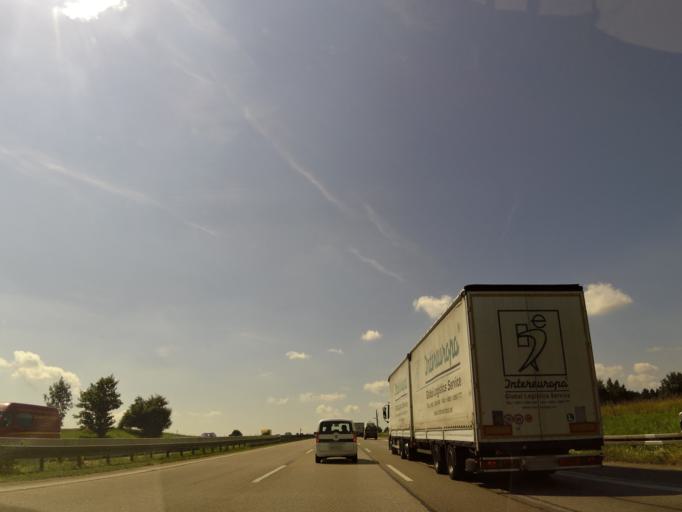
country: DE
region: Bavaria
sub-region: Upper Bavaria
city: Schweitenkirchen
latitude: 48.5457
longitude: 11.5939
